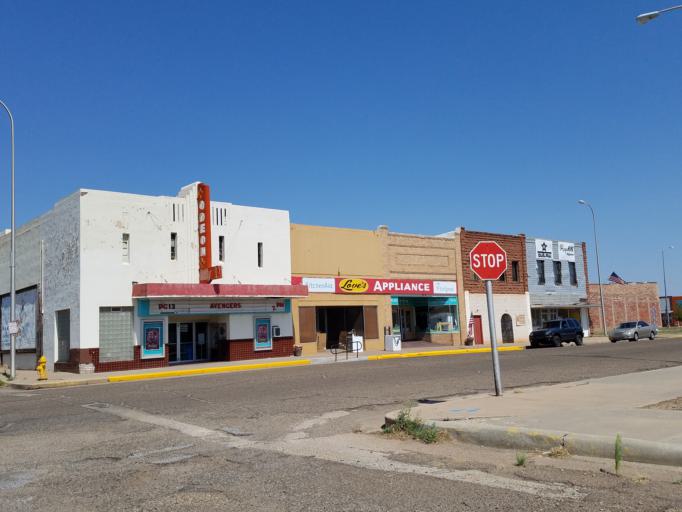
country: US
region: New Mexico
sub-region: Quay County
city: Tucumcari
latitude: 35.1781
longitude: -103.7258
